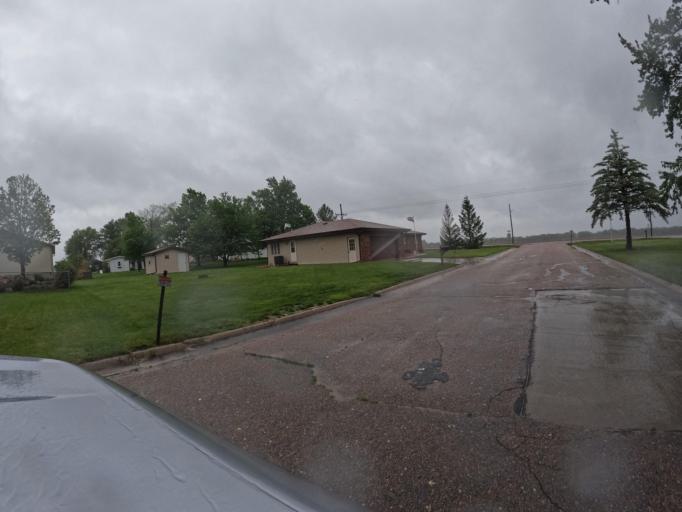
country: US
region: Nebraska
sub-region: Gage County
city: Wymore
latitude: 40.1245
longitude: -96.6771
